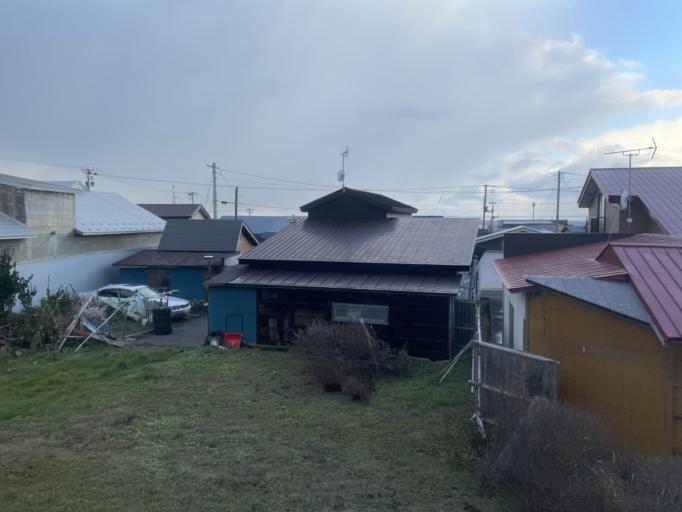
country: JP
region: Aomori
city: Mutsu
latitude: 41.0897
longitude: 141.2496
